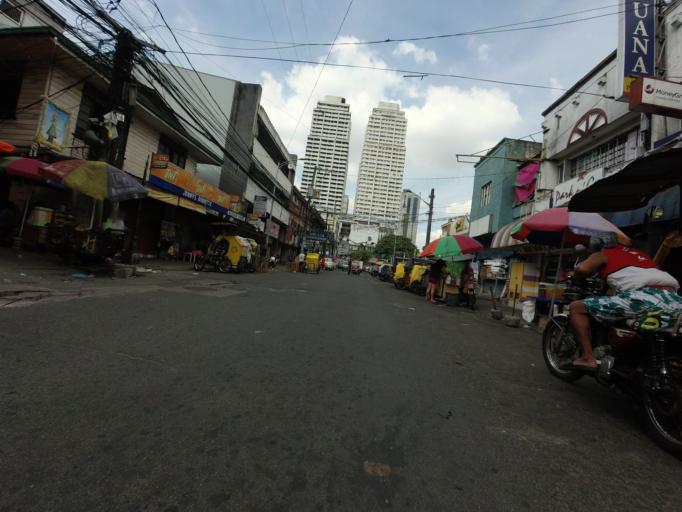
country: PH
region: Metro Manila
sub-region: City of Manila
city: Port Area
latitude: 14.5692
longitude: 120.9889
